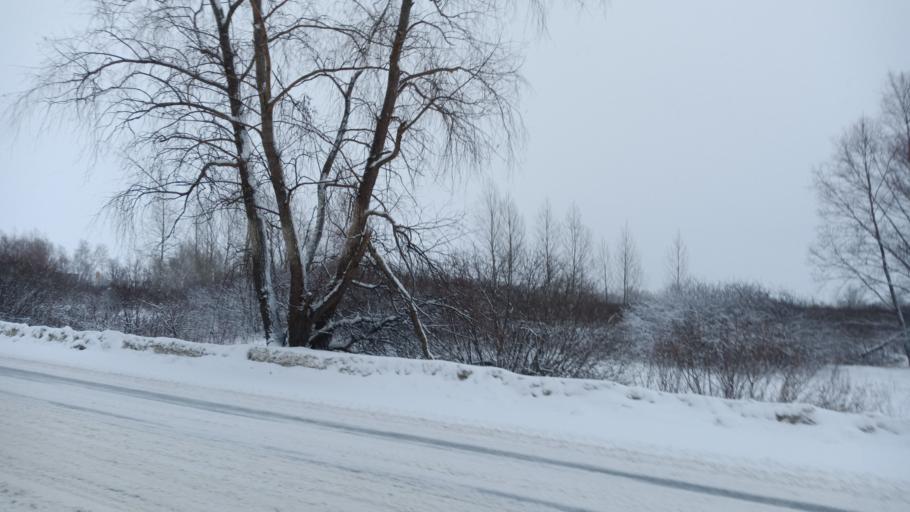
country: RU
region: Altai Krai
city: Zaton
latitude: 53.3119
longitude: 83.8309
